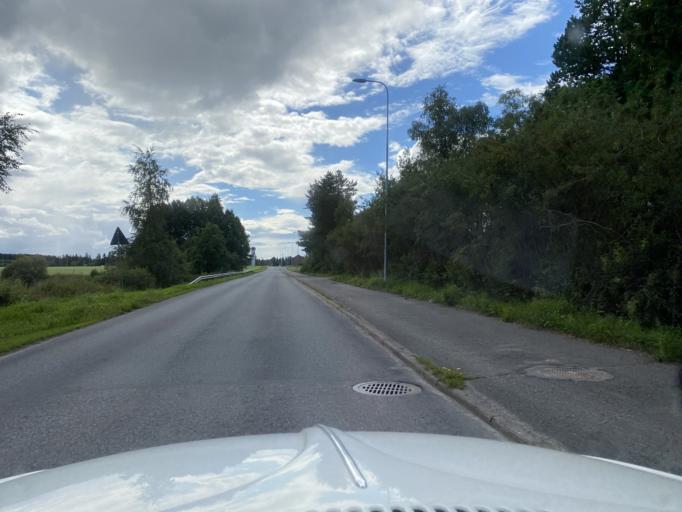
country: FI
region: Satakunta
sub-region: Pori
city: Huittinen
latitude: 61.1719
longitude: 22.6881
